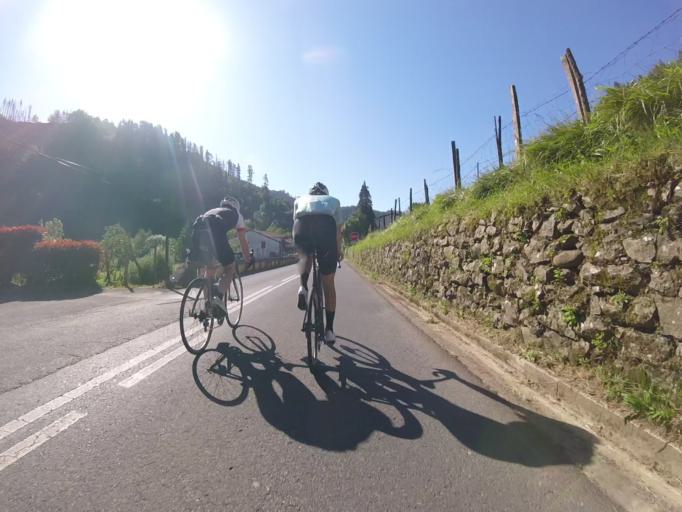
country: ES
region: Basque Country
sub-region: Provincia de Guipuzcoa
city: Azpeitia
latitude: 43.1514
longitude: -2.2390
